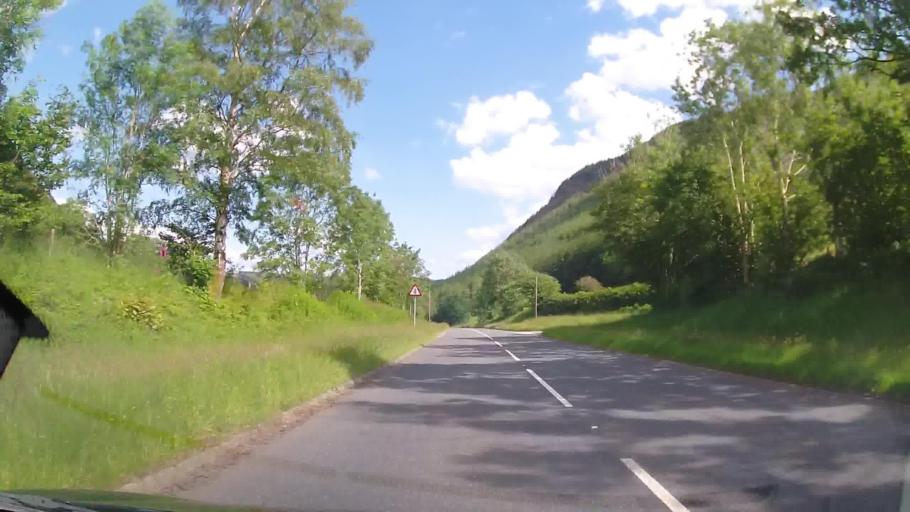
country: GB
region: Wales
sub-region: Gwynedd
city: Corris
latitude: 52.7250
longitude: -3.7081
